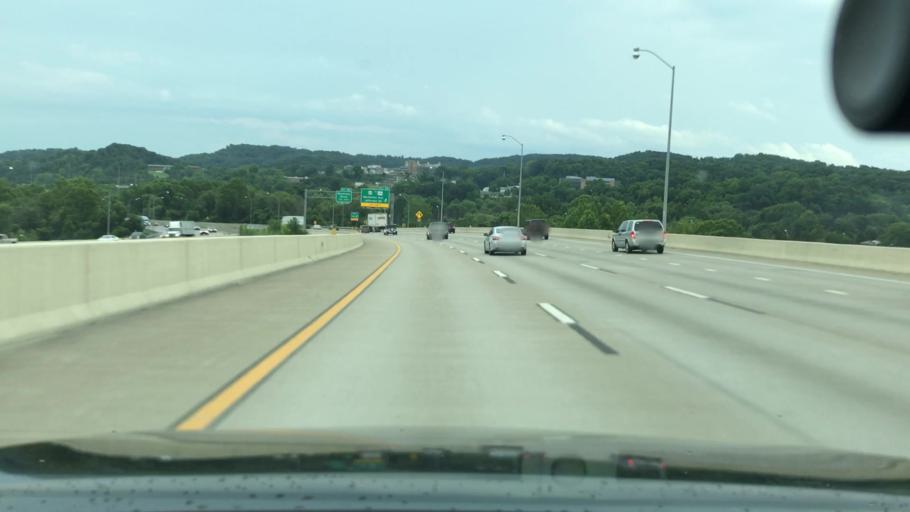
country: US
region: West Virginia
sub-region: Kanawha County
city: Dunbar
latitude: 38.3605
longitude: -81.7179
